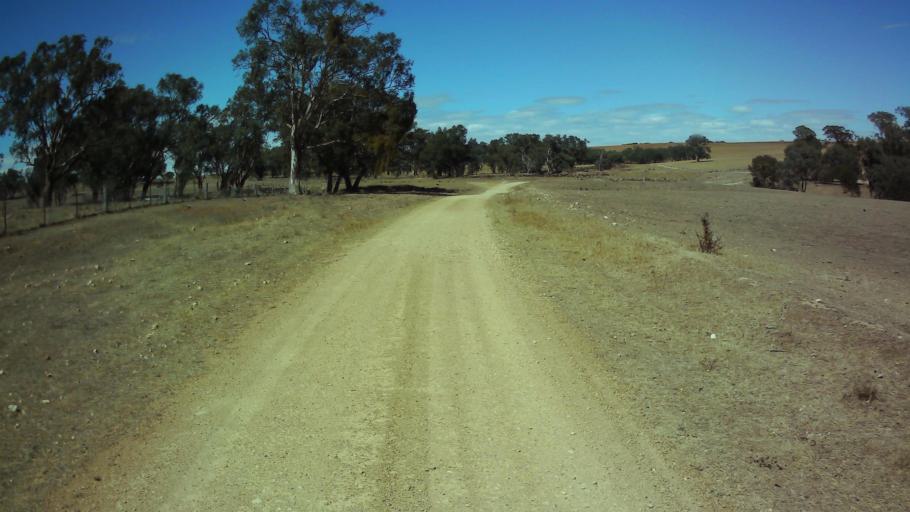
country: AU
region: New South Wales
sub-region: Young
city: Young
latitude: -34.0439
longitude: 148.4266
